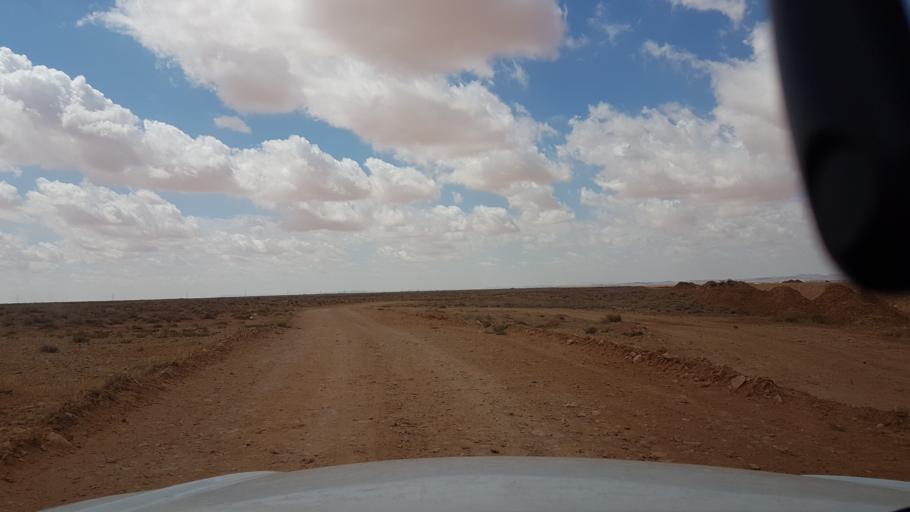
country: TN
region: Madanin
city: Medenine
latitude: 33.2724
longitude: 10.5889
